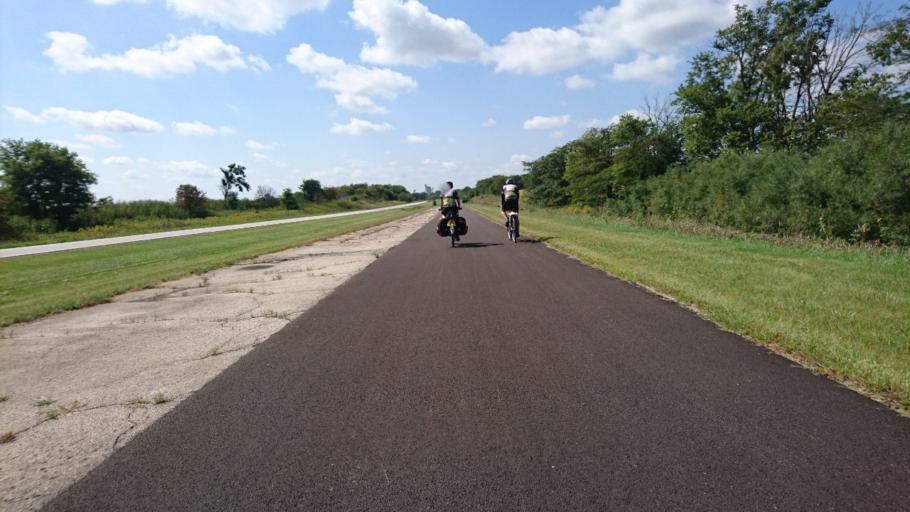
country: US
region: Illinois
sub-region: McLean County
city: Hudson
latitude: 40.5755
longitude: -88.8814
